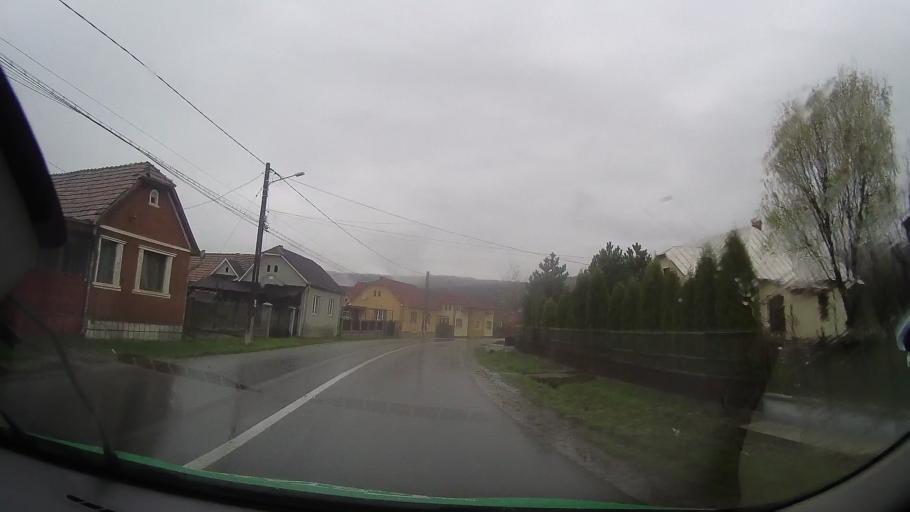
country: RO
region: Bistrita-Nasaud
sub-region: Comuna Mariselu
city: Mariselu
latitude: 47.0133
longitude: 24.5544
